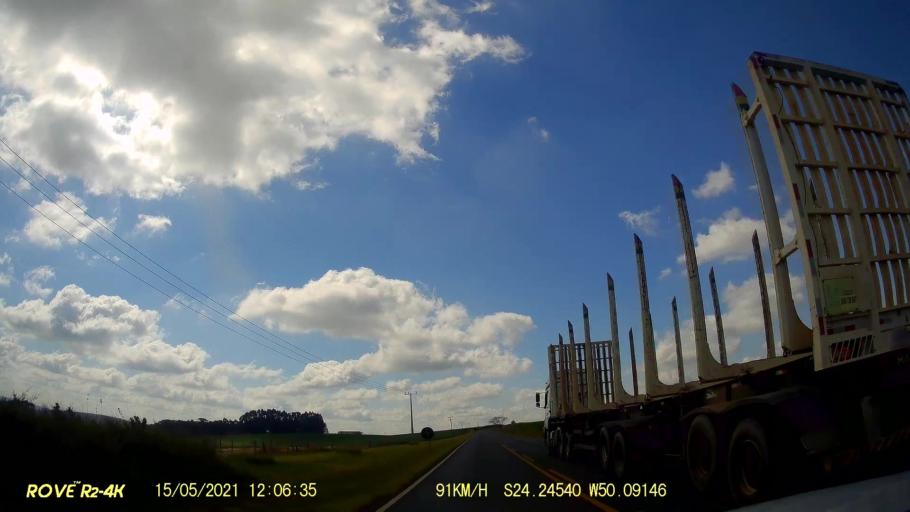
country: BR
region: Parana
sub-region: Pirai Do Sul
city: Pirai do Sul
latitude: -24.2454
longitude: -50.0914
